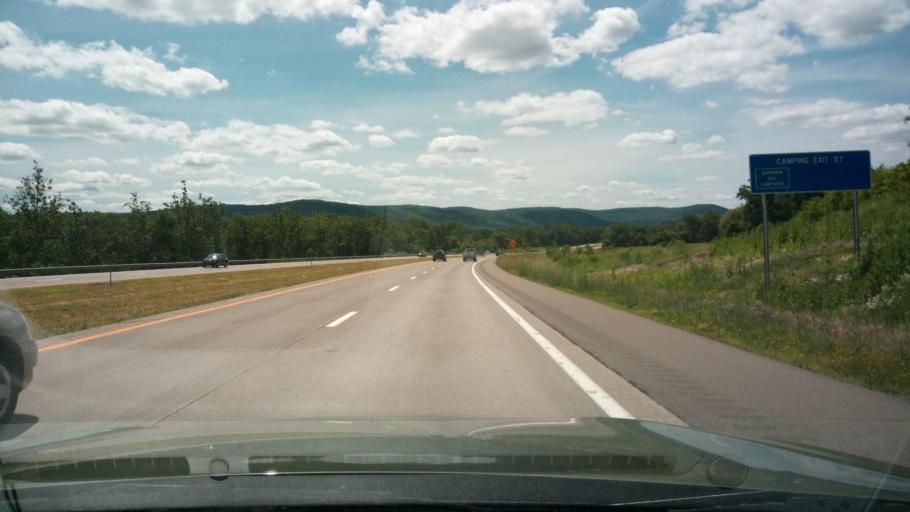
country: US
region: New York
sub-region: Chemung County
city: Southport
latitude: 42.0256
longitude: -76.7055
